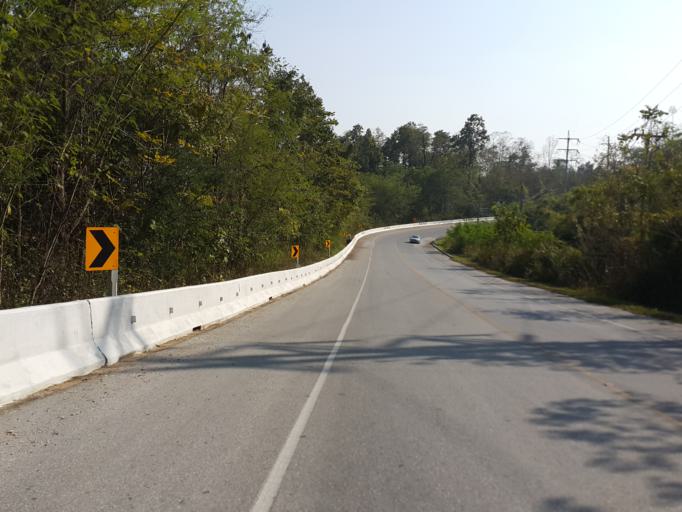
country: TH
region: Lampang
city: Chae Hom
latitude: 18.5959
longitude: 99.5491
